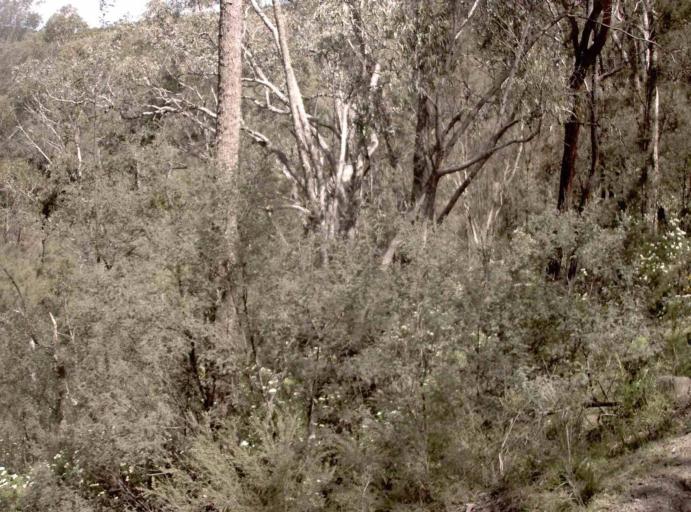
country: AU
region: New South Wales
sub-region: Bombala
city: Bombala
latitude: -37.1080
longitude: 148.6408
